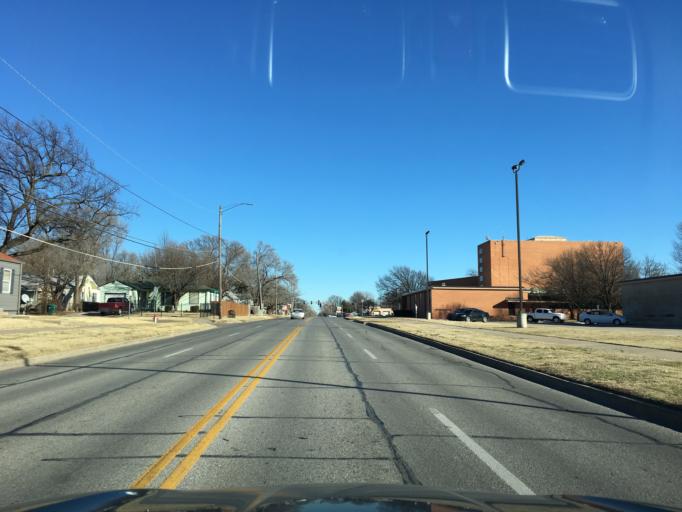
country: US
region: Kansas
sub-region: Sedgwick County
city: Wichita
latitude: 37.6719
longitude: -97.2744
